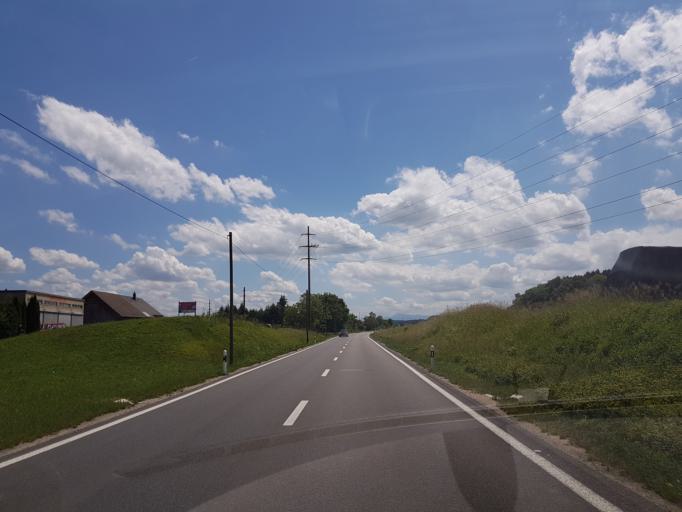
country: CH
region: Aargau
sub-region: Bezirk Baden
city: Mellingen
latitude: 47.4020
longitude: 8.2868
